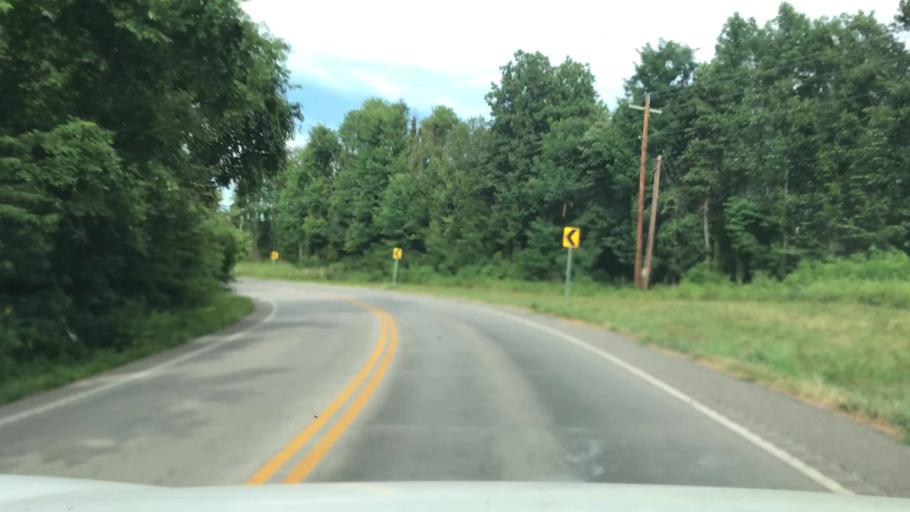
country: US
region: Missouri
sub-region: Saint Charles County
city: Weldon Spring
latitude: 38.6631
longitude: -90.7418
